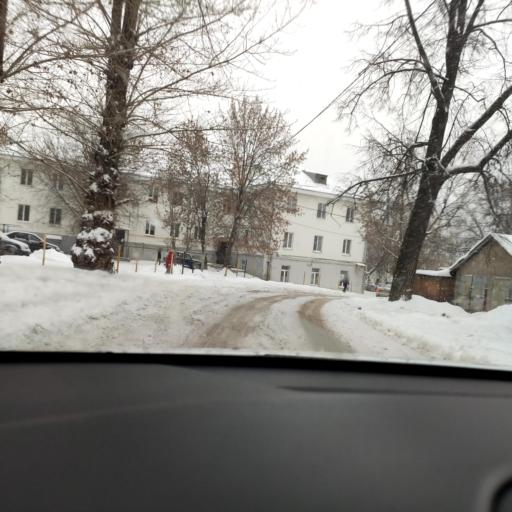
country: RU
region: Tatarstan
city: Vysokaya Gora
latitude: 55.8663
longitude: 49.2327
